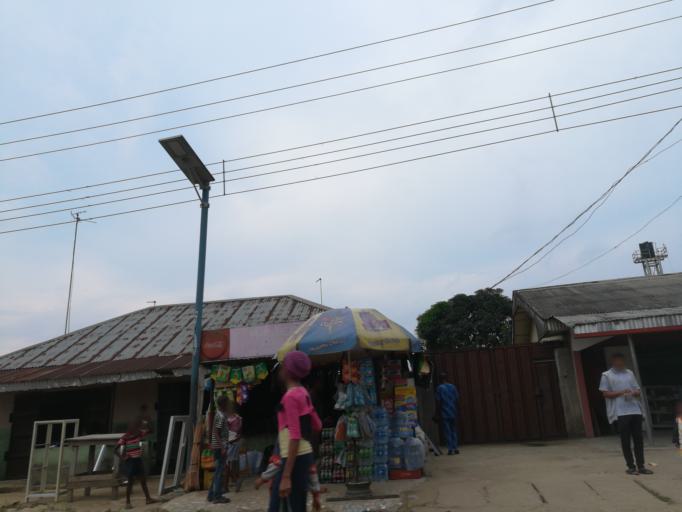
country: NG
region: Rivers
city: Okrika
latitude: 4.7839
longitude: 7.1298
